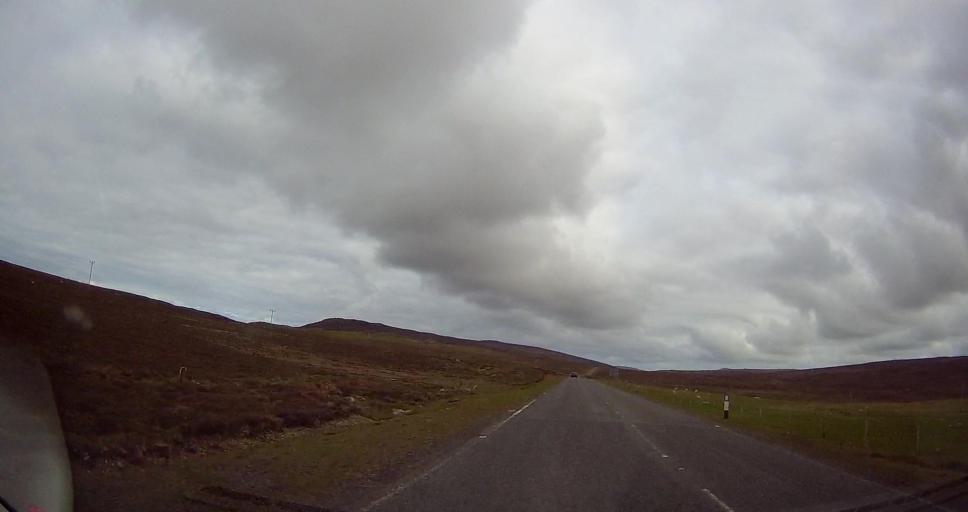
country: GB
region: Scotland
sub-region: Shetland Islands
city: Shetland
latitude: 60.7000
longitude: -0.9205
